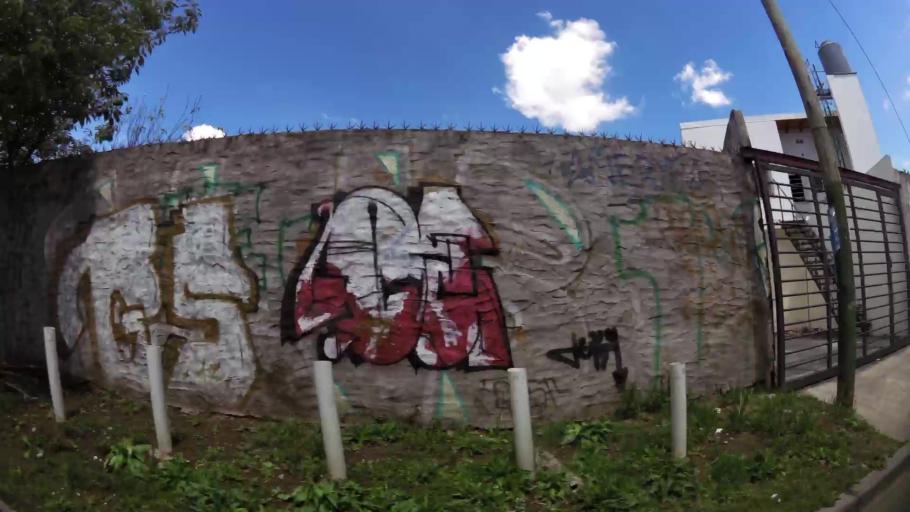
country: AR
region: Buenos Aires
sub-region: Partido de Lomas de Zamora
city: Lomas de Zamora
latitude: -34.7354
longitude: -58.4197
